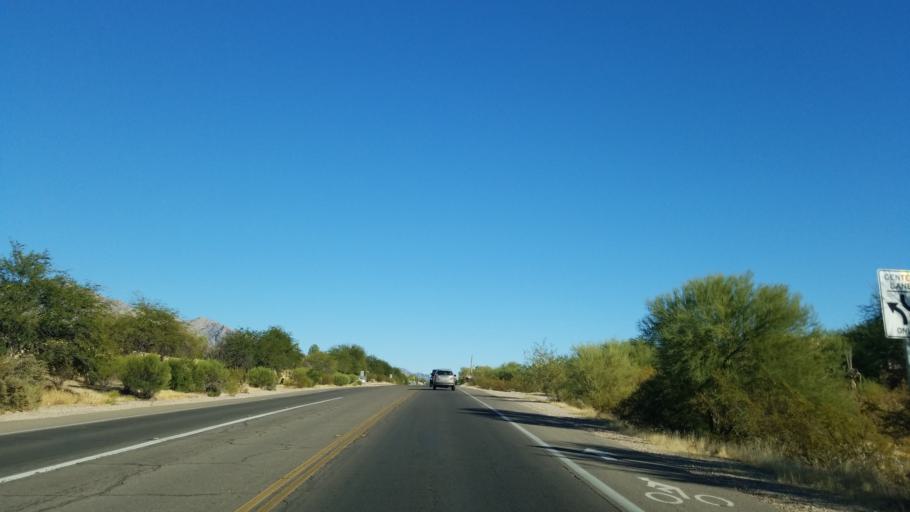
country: US
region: Arizona
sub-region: Pima County
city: Casas Adobes
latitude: 32.3228
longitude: -110.9659
